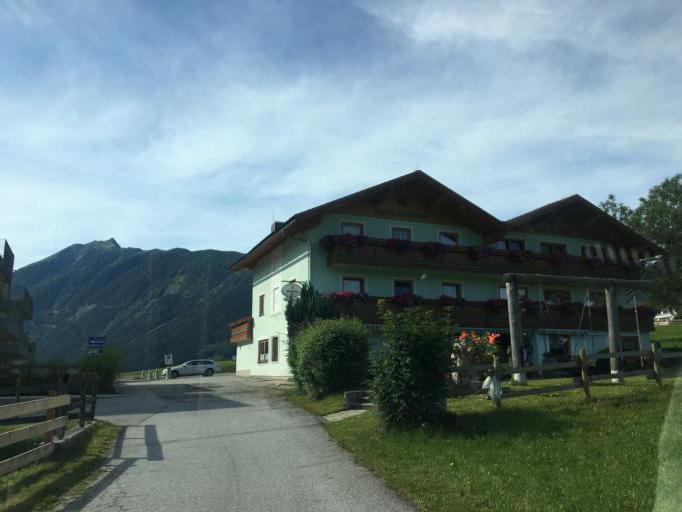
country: AT
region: Styria
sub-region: Politischer Bezirk Liezen
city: Schladming
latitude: 47.3820
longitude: 13.6678
